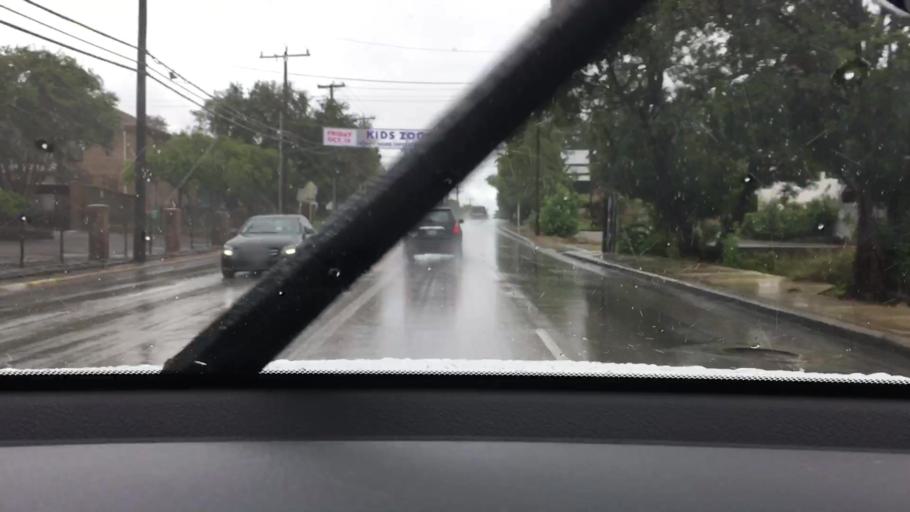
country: US
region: Texas
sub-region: Bexar County
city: Alamo Heights
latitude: 29.5062
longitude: -98.4663
